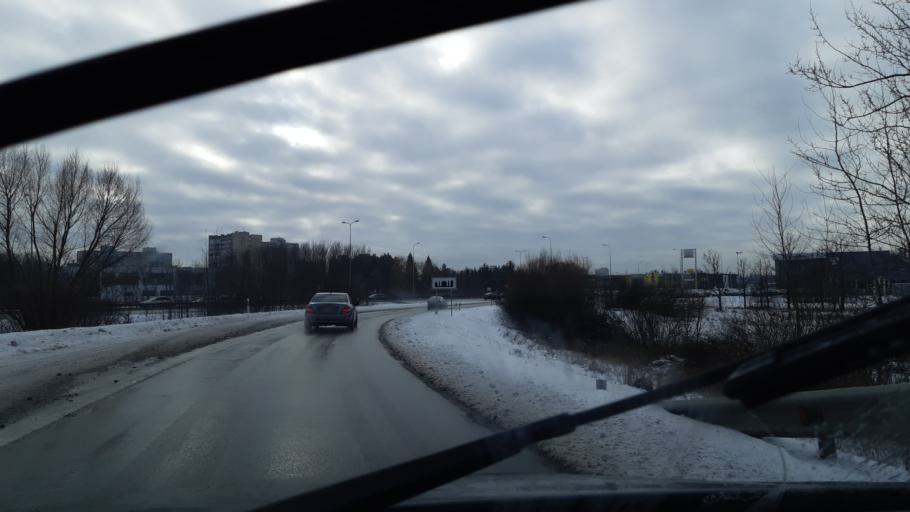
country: LT
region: Kauno apskritis
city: Dainava (Kaunas)
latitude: 54.9323
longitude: 23.9783
